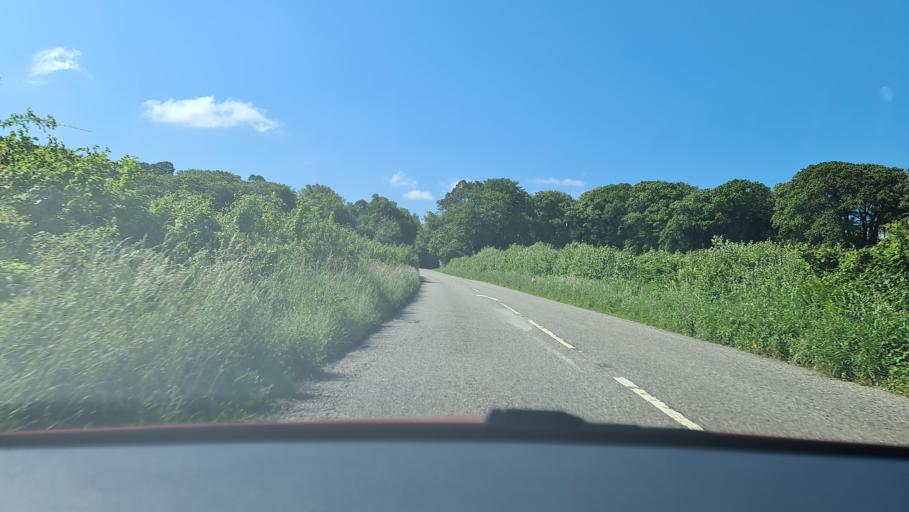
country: GB
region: England
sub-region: Cornwall
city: Lostwithiel
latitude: 50.4261
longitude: -4.6423
